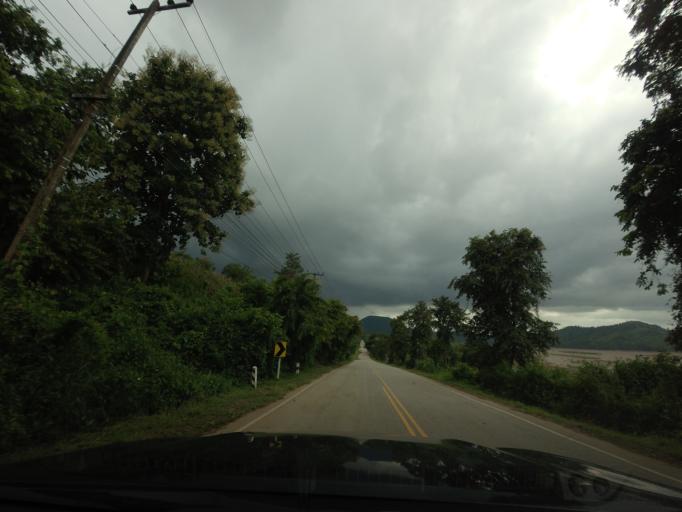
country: LA
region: Vientiane
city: Muang Sanakham
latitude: 17.9656
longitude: 101.7462
